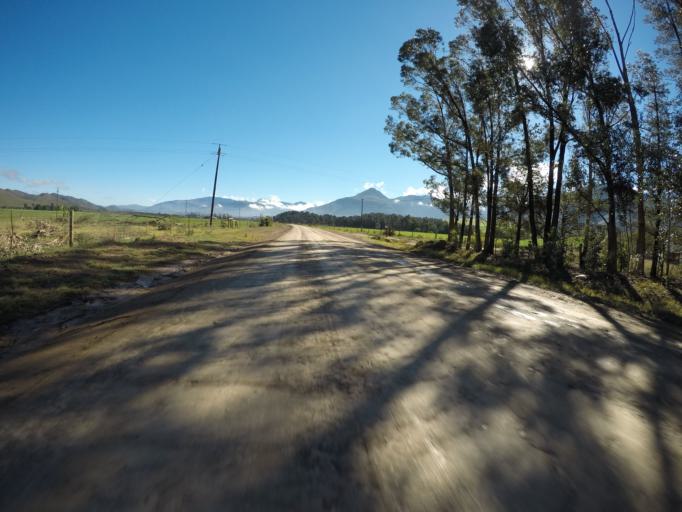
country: ZA
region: Western Cape
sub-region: Overberg District Municipality
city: Caledon
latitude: -34.0742
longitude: 19.6404
